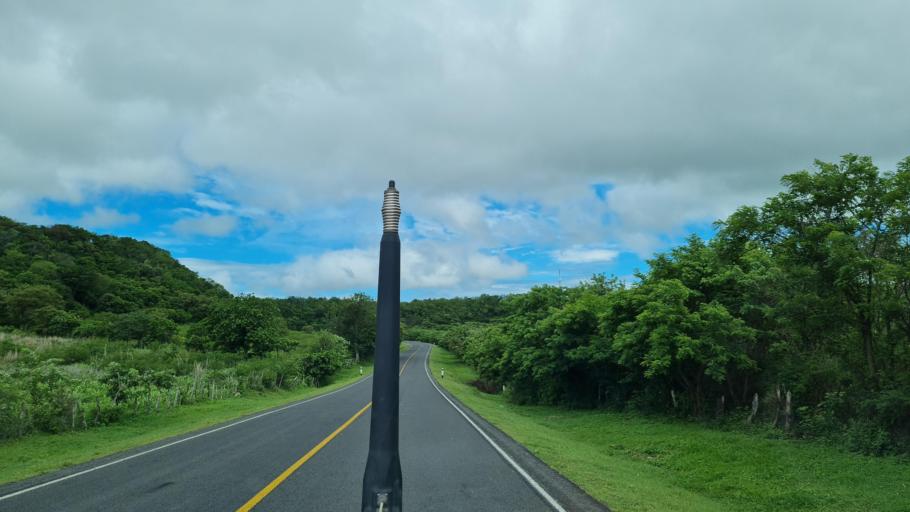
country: NI
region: Matagalpa
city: Terrabona
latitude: 12.5825
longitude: -85.9763
